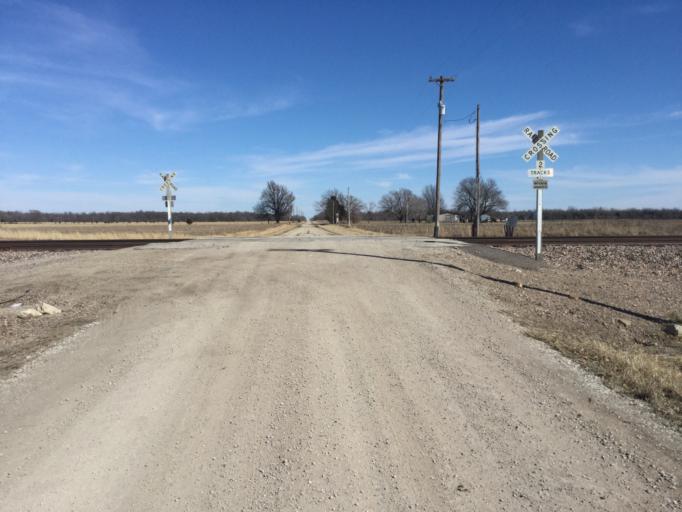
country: US
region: Kansas
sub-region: Cherokee County
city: Columbus
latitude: 37.2665
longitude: -94.8257
